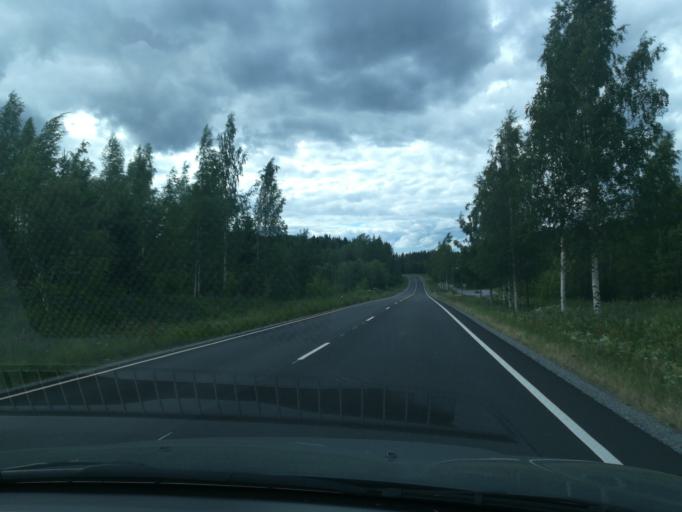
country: FI
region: Southern Savonia
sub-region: Mikkeli
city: Mikkeli
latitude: 61.6586
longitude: 27.1190
